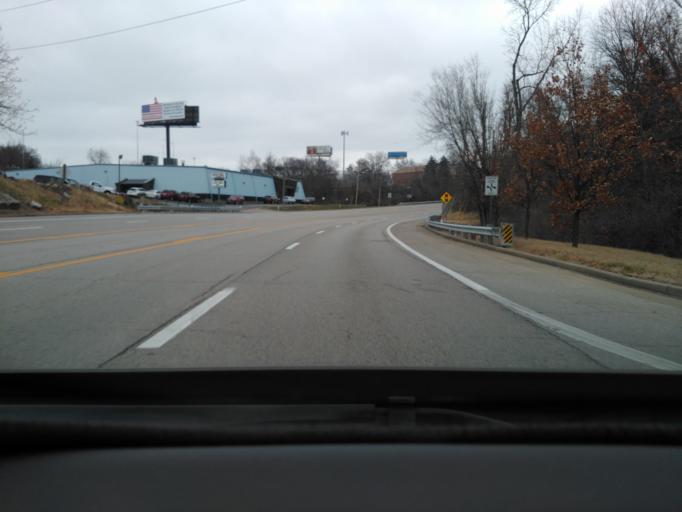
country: US
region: Missouri
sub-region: Saint Louis County
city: Mehlville
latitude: 38.4973
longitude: -90.3419
